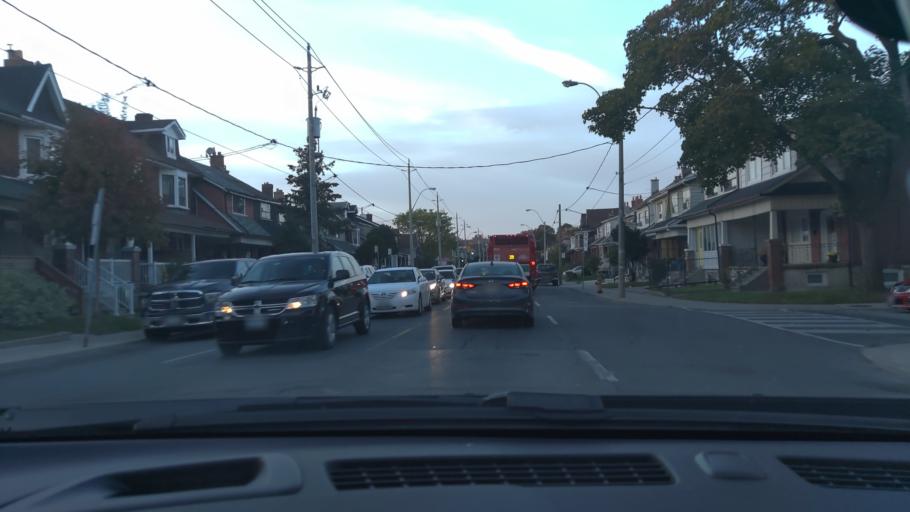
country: CA
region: Ontario
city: Toronto
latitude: 43.6811
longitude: -79.4443
